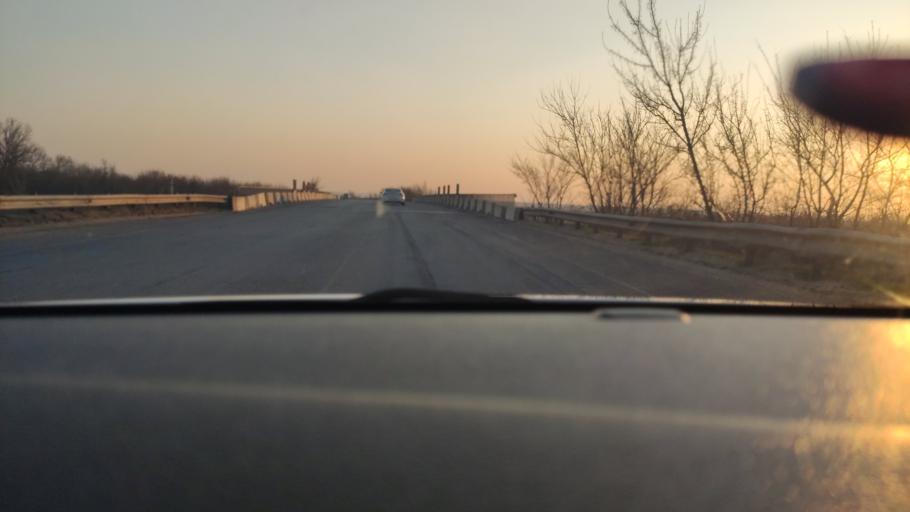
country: RU
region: Voronezj
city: Kolodeznyy
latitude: 51.4097
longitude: 39.2487
